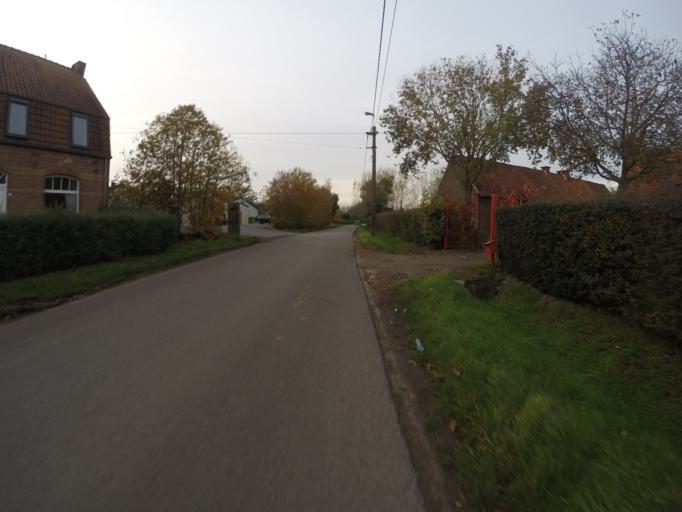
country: BE
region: Flanders
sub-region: Provincie Oost-Vlaanderen
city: Aalter
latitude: 51.0999
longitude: 3.4701
